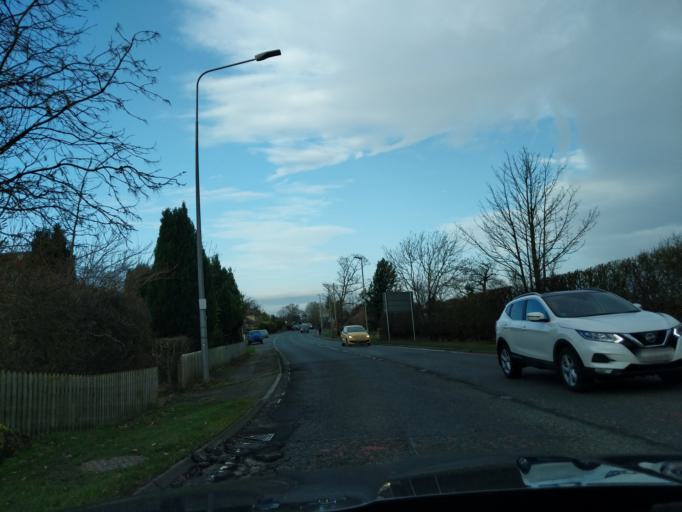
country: GB
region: England
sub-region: Northumberland
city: Ponteland
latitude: 55.0432
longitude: -1.7255
